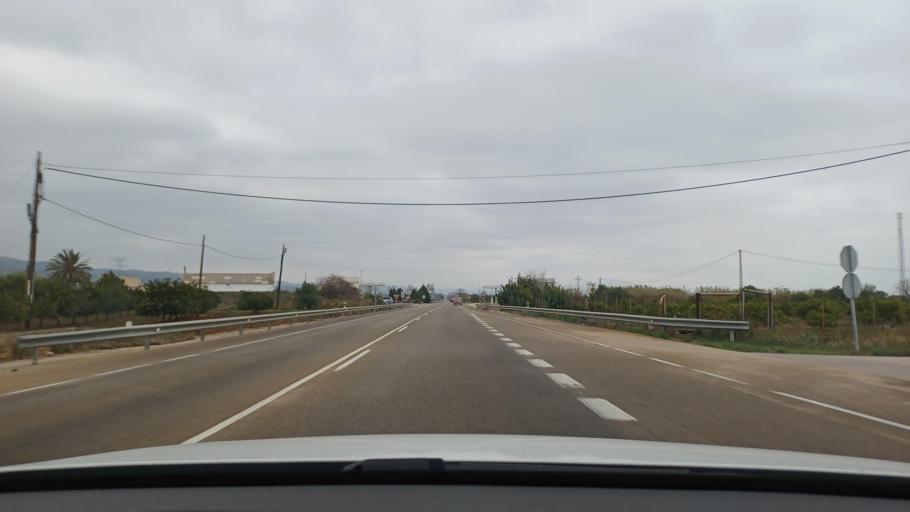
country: ES
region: Valencia
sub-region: Provincia de Castello
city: Orpesa/Oropesa del Mar
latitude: 40.1330
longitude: 0.1486
